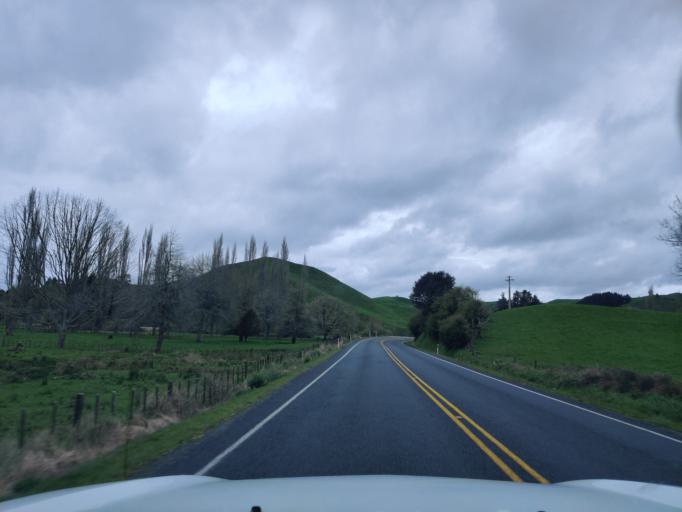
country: NZ
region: Waikato
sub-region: Otorohanga District
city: Otorohanga
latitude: -38.5253
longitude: 175.1755
